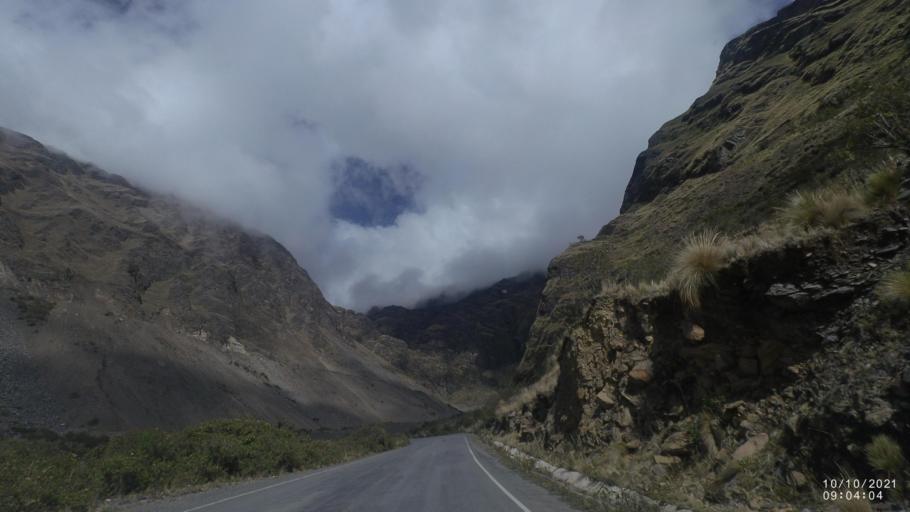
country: BO
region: La Paz
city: Quime
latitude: -17.0020
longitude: -67.2743
